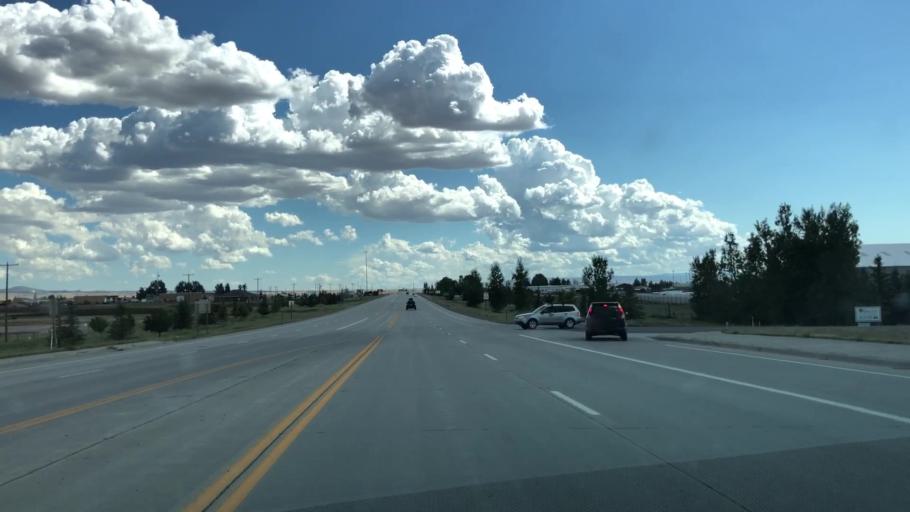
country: US
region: Wyoming
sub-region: Albany County
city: Laramie
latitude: 41.2893
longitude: -105.5923
